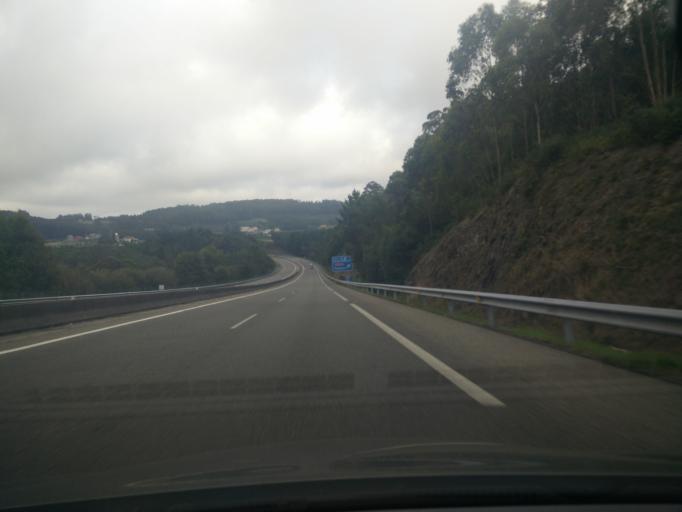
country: ES
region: Galicia
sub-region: Provincia da Coruna
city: Laracha
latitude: 43.2676
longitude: -8.5559
